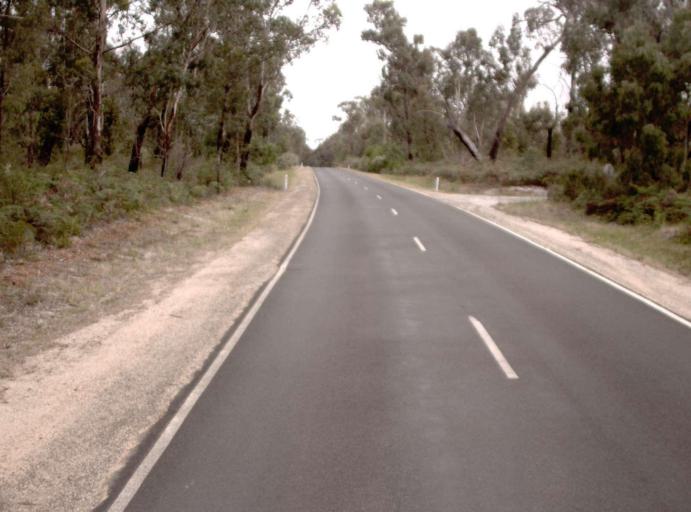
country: AU
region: Victoria
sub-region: Latrobe
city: Traralgon
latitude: -38.4609
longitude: 146.8209
